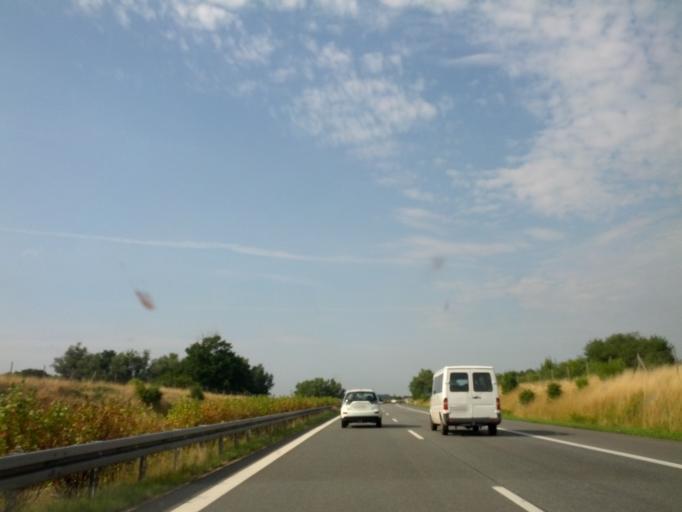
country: DE
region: Mecklenburg-Vorpommern
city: Krakow am See
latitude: 53.6612
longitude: 12.3632
